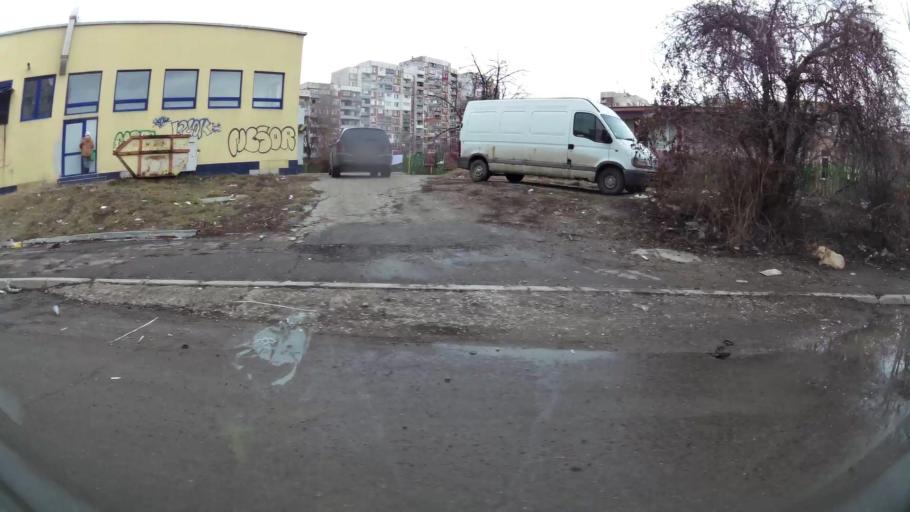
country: BG
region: Sofiya
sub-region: Obshtina Bozhurishte
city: Bozhurishte
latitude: 42.7294
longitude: 23.2495
